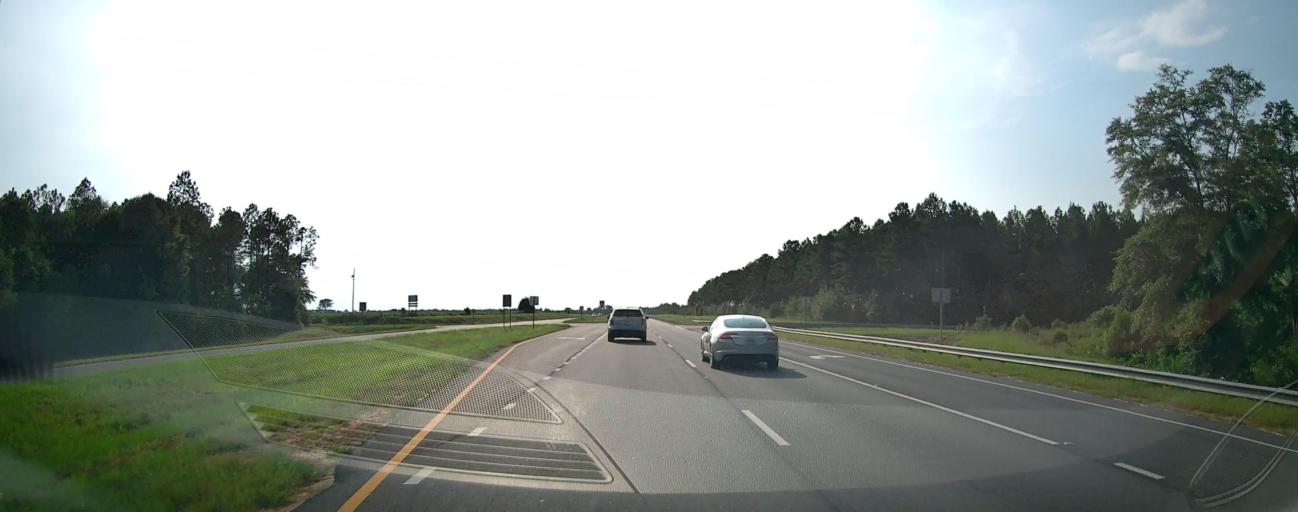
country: US
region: Georgia
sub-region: Taylor County
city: Butler
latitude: 32.5468
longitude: -84.2498
